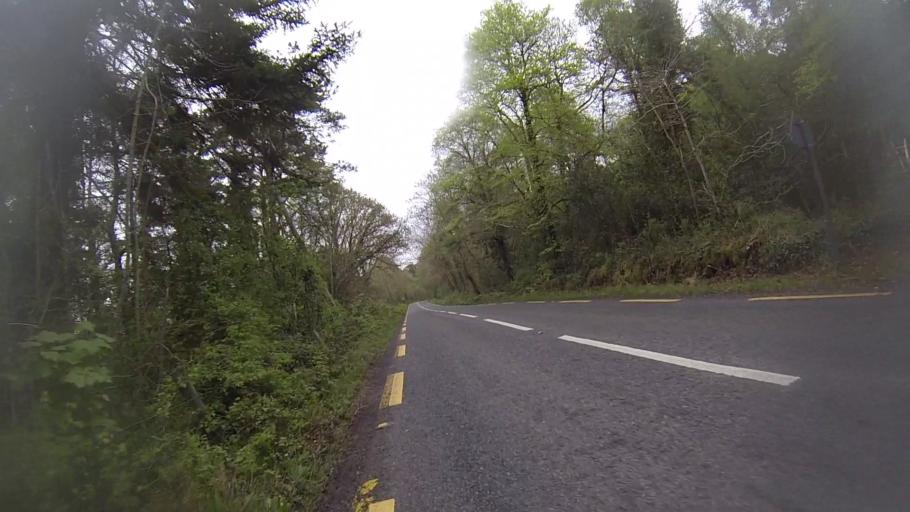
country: IE
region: Munster
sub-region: Ciarrai
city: Kenmare
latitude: 51.8718
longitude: -9.5602
